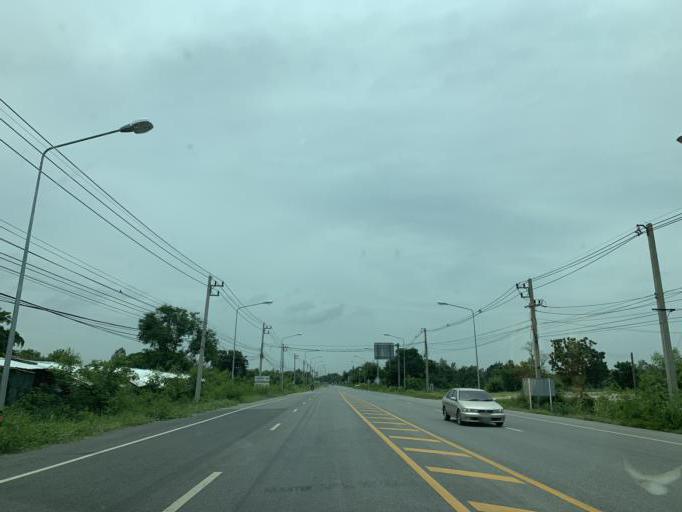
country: TH
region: Uthai Thani
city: Uthai Thani
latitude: 15.4044
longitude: 100.0225
